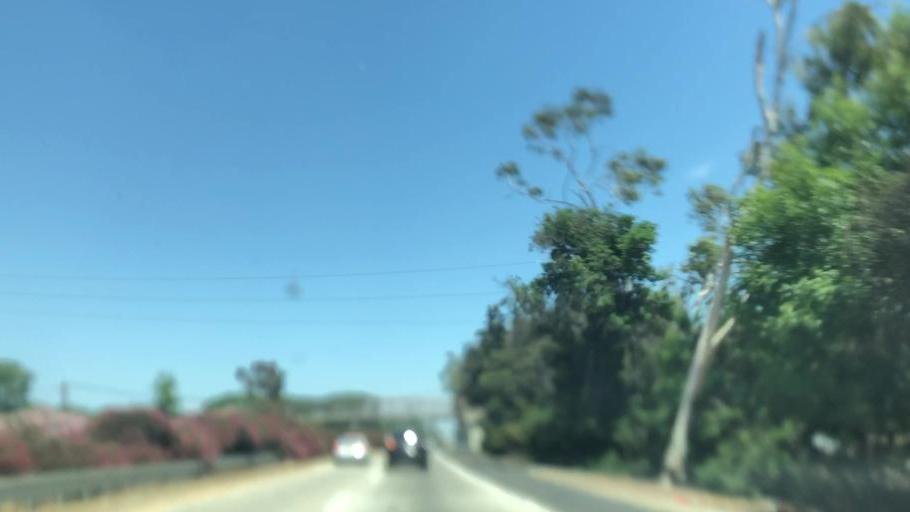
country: US
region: California
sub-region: Ventura County
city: El Rio
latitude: 34.2720
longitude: -119.2087
